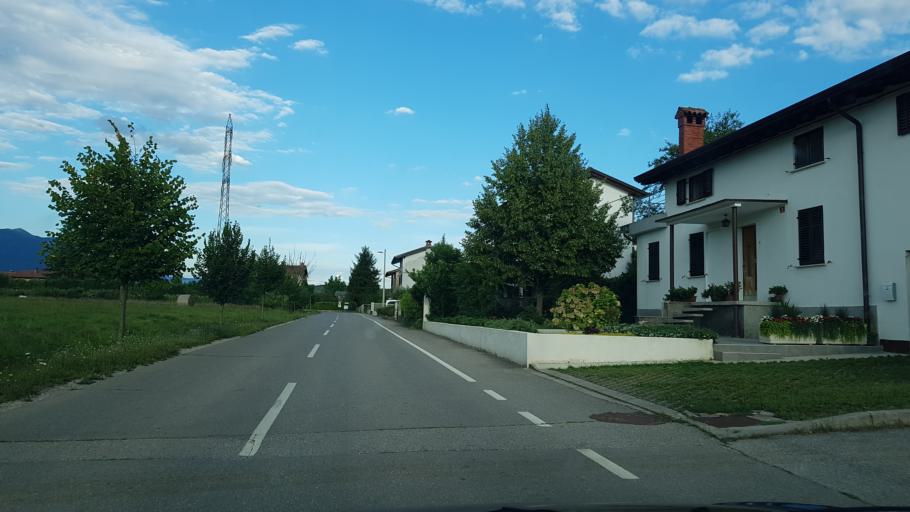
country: SI
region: Rence-Vogrsko
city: Rence
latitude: 45.8877
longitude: 13.6657
